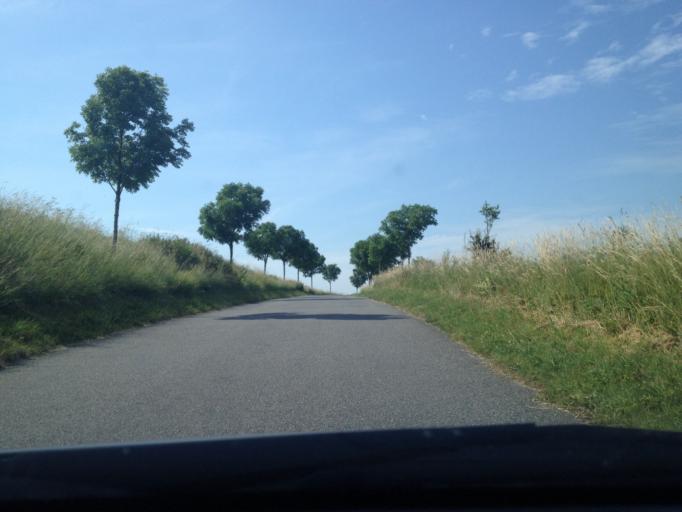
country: DK
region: Central Jutland
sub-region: Samso Kommune
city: Tranebjerg
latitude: 55.7914
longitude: 10.5745
